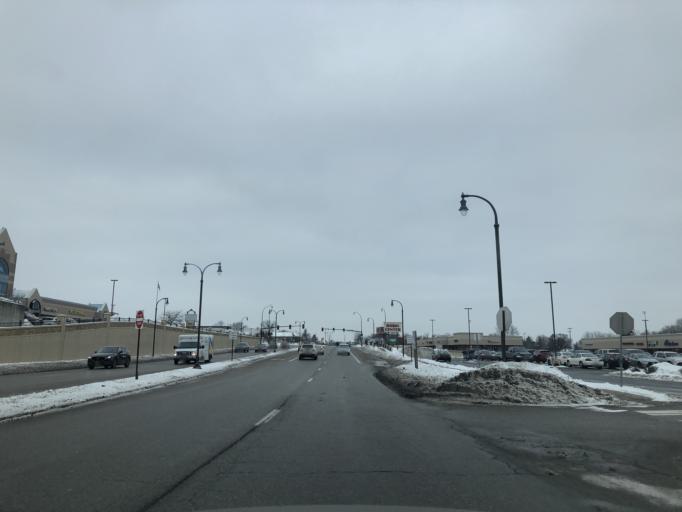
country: US
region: Minnesota
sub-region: Hennepin County
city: Robbinsdale
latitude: 45.0292
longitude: -93.3346
